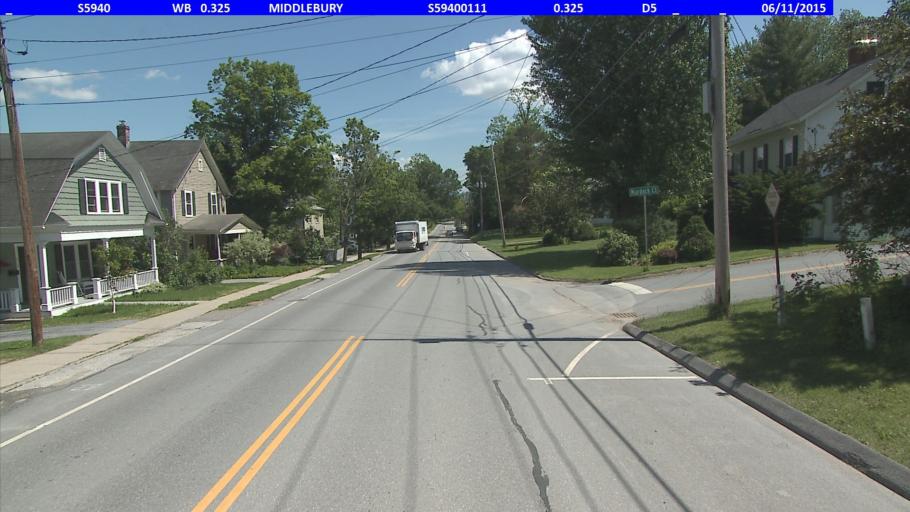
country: US
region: Vermont
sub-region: Addison County
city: Middlebury (village)
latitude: 44.0150
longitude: -73.1758
